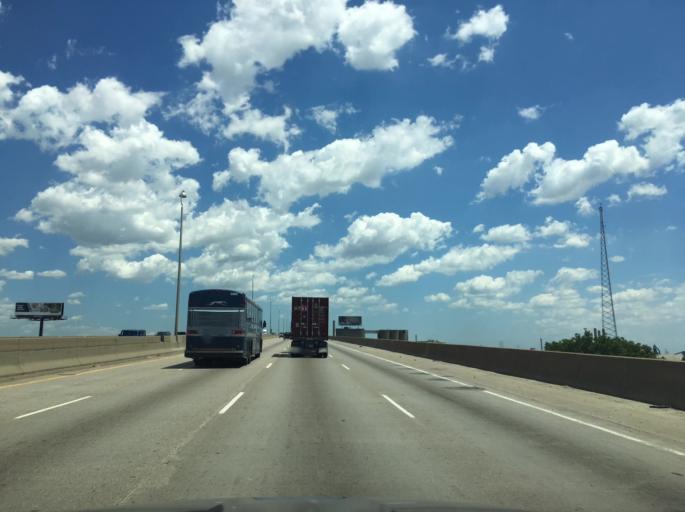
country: US
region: Michigan
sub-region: Wayne County
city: River Rouge
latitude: 42.2846
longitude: -83.1448
